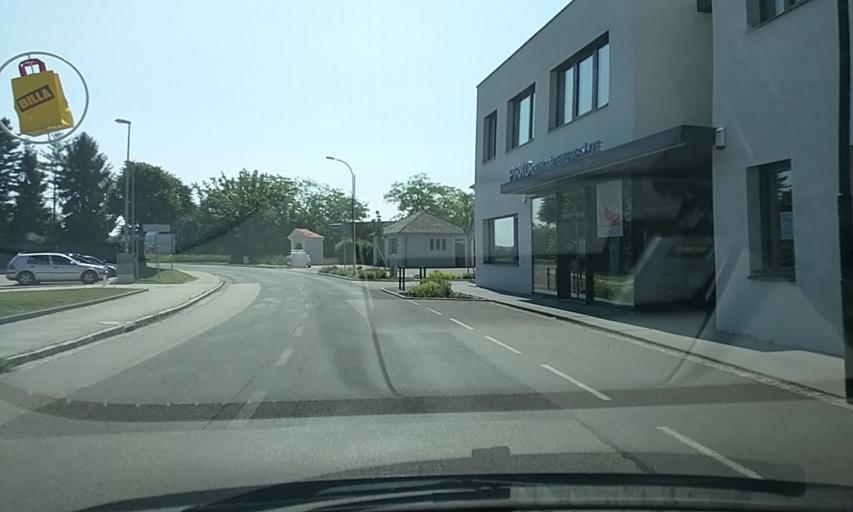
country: AT
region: Lower Austria
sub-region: Politischer Bezirk Krems
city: Weinzierl bei Krems
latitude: 48.3919
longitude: 15.5813
